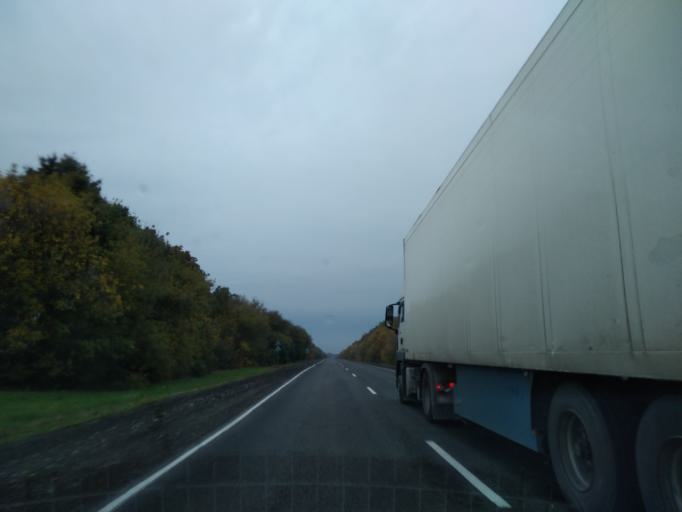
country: RU
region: Lipetsk
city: Zadonsk
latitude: 52.4624
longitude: 38.7741
